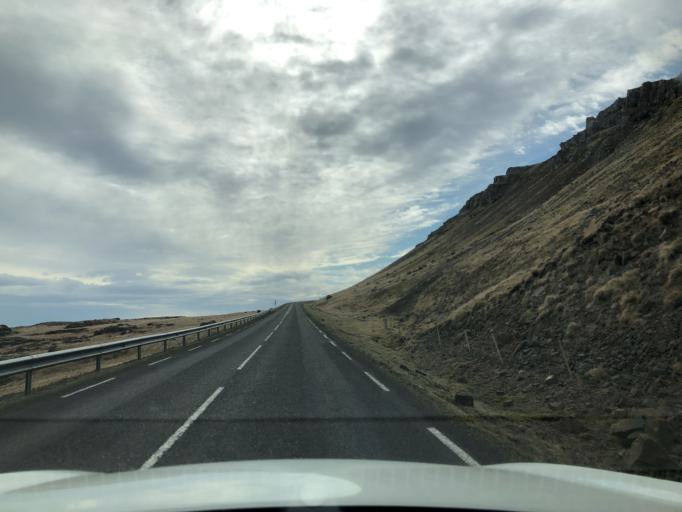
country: IS
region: East
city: Eskifjoerdur
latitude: 64.7404
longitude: -13.9980
